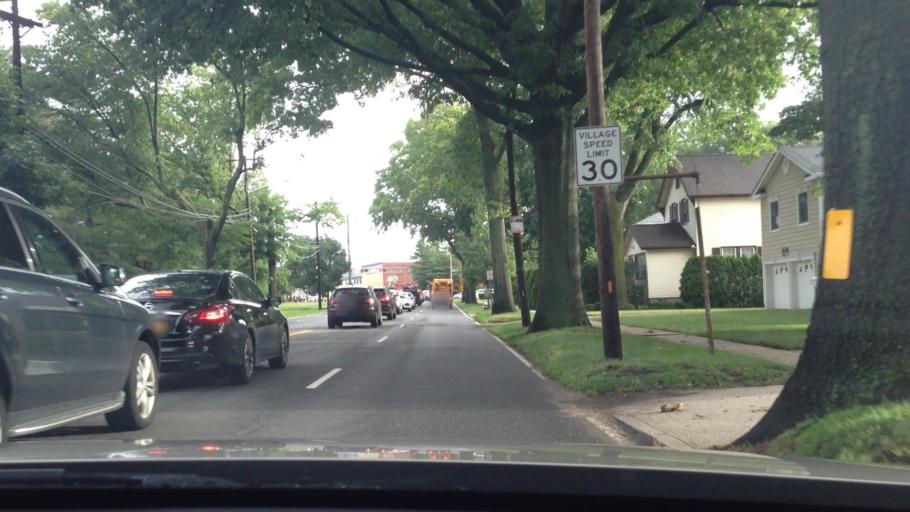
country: US
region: New York
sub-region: Nassau County
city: New Hyde Park
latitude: 40.7294
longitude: -73.6790
